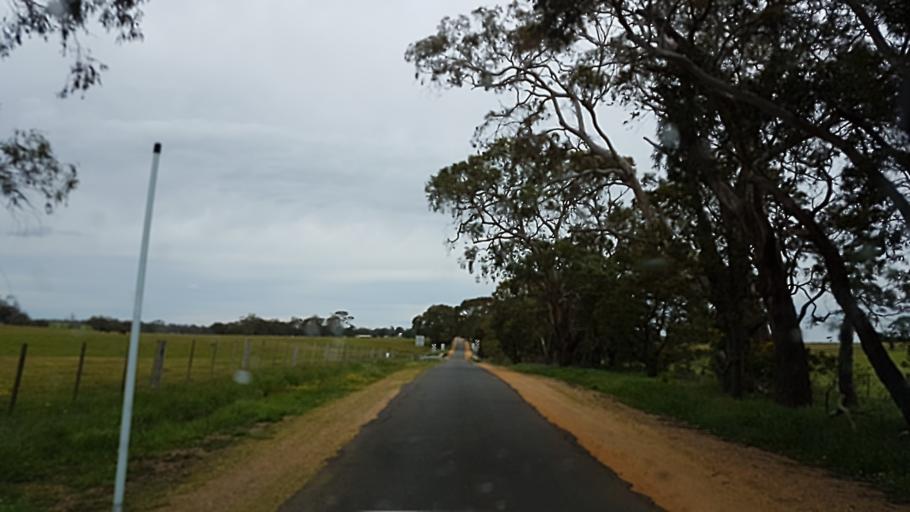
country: AU
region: Victoria
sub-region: Ballarat North
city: Mount Clear
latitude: -37.7768
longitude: 144.0561
